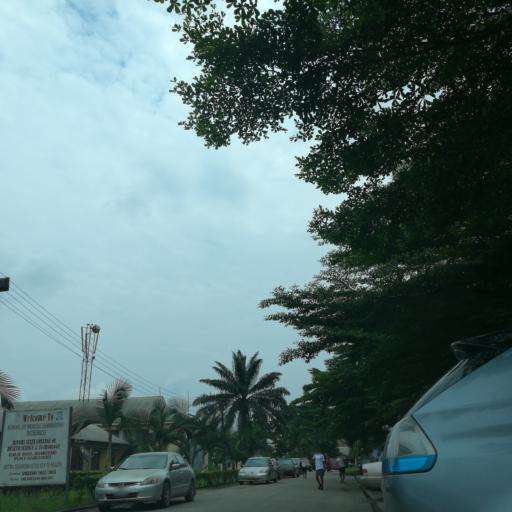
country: NG
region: Rivers
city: Port Harcourt
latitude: 4.8184
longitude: 6.9836
